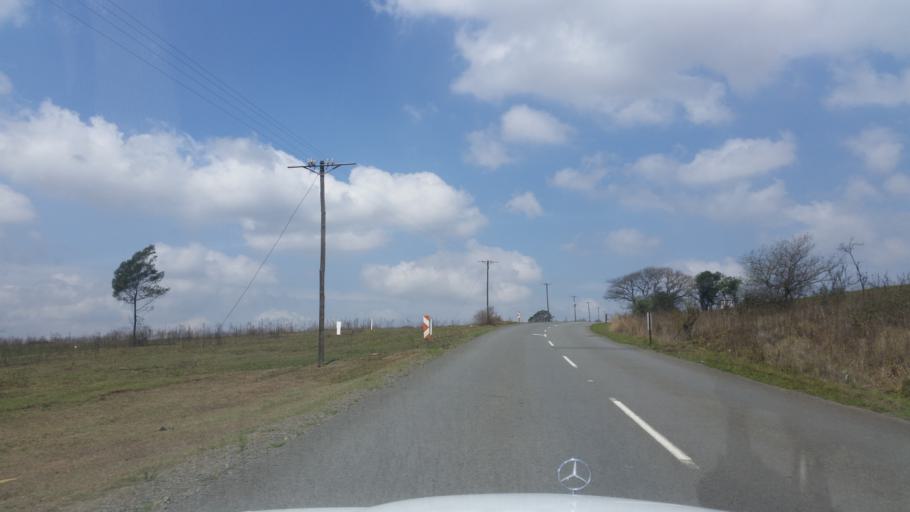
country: ZA
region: KwaZulu-Natal
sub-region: uMgungundlovu District Municipality
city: Camperdown
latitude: -29.7051
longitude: 30.4949
